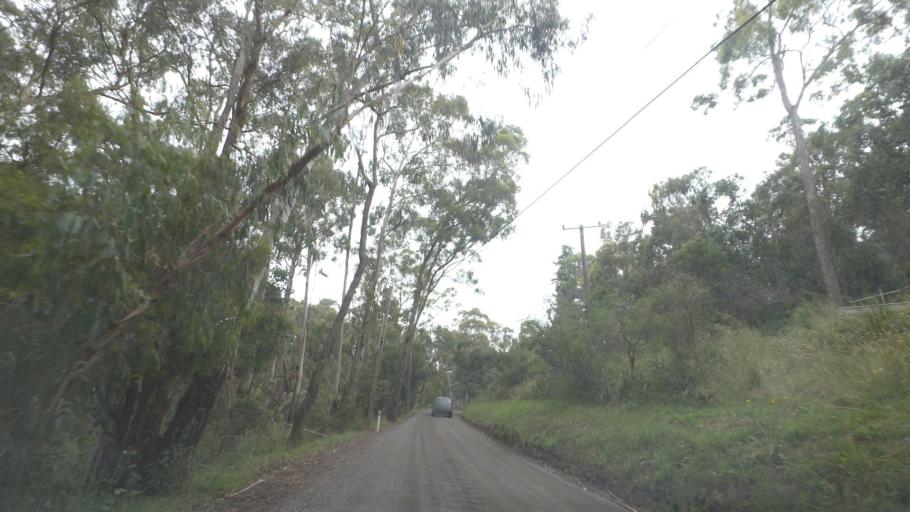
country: AU
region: Victoria
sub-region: Manningham
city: Warrandyte
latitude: -37.7571
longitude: 145.2263
